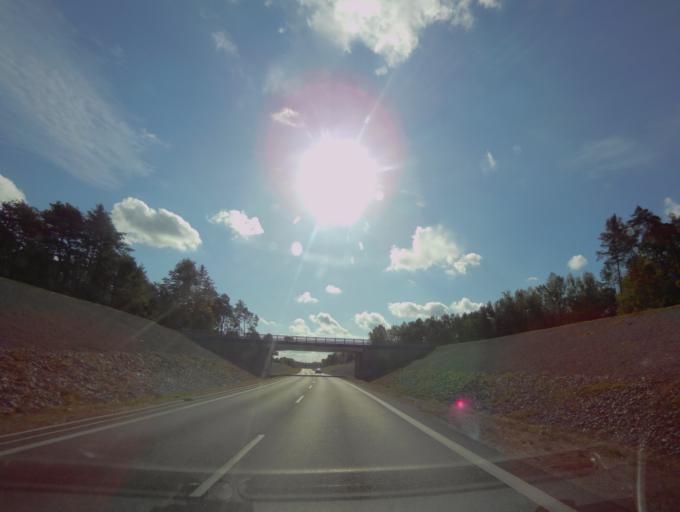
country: PL
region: Subcarpathian Voivodeship
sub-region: Powiat lezajski
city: Lezajsk
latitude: 50.2612
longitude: 22.3961
